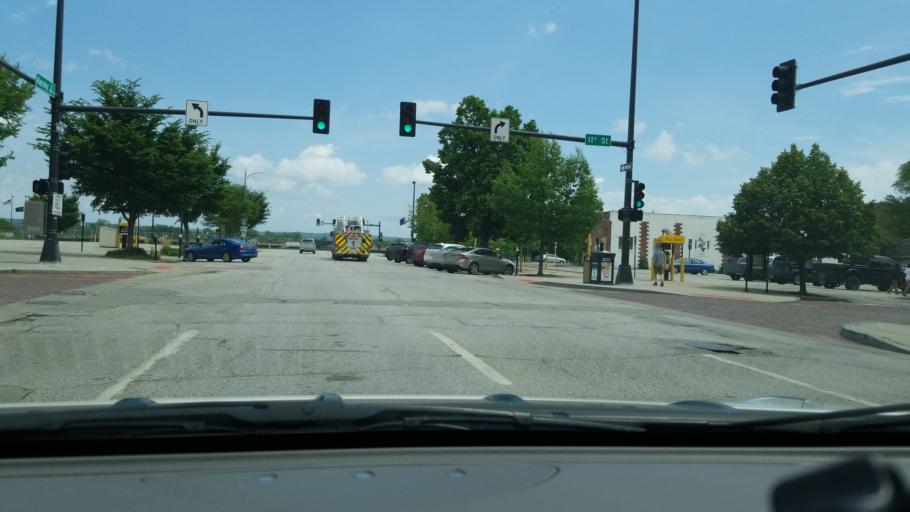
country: US
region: Nebraska
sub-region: Douglas County
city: Omaha
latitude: 41.2565
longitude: -95.9308
